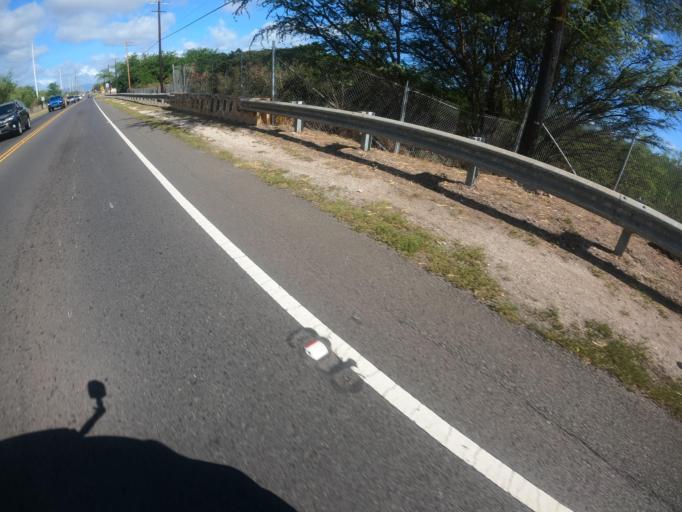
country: US
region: Hawaii
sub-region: Honolulu County
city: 'Ewa Villages
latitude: 21.3253
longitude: -158.0662
